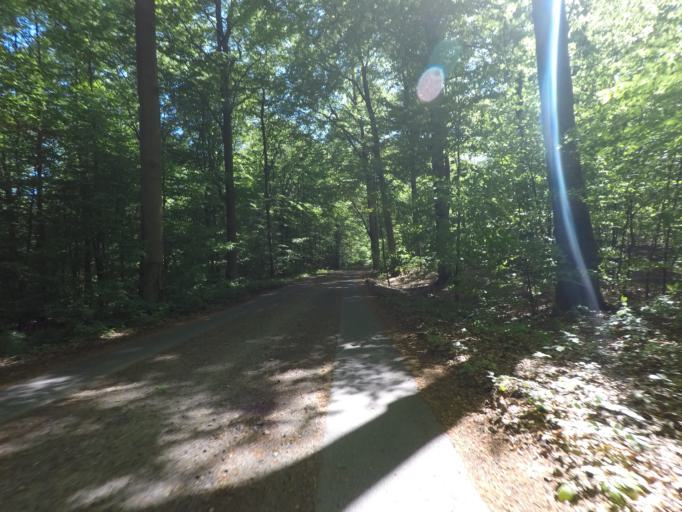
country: DE
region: Brandenburg
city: Eberswalde
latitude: 52.8185
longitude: 13.7794
